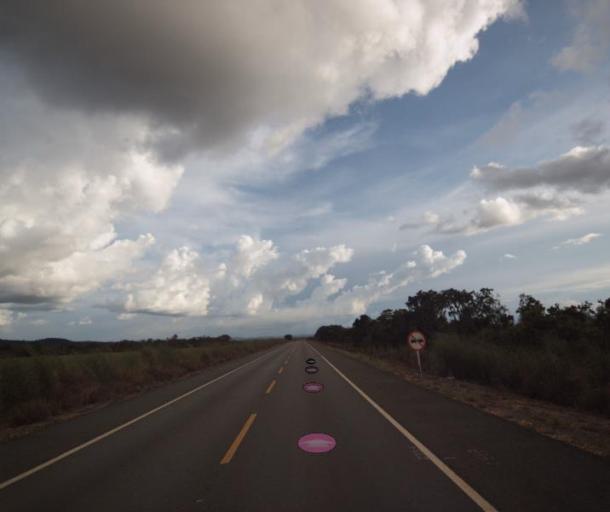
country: BR
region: Goias
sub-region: Niquelandia
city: Niquelandia
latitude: -14.7120
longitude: -48.6057
